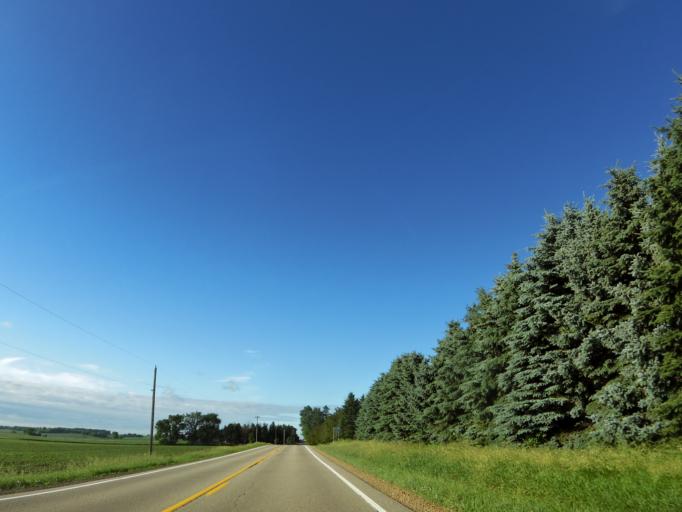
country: US
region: Minnesota
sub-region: Dakota County
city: Hastings
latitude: 44.8139
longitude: -92.8629
